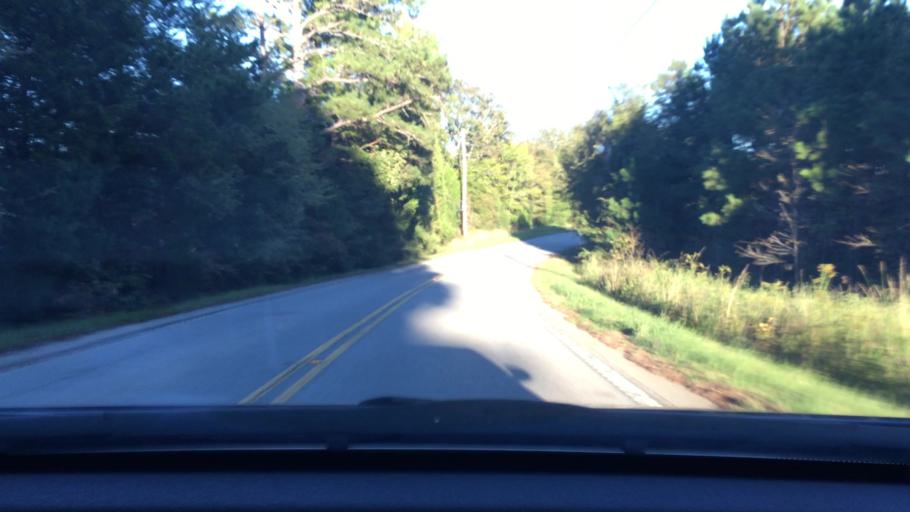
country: US
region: South Carolina
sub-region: Lexington County
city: Irmo
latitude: 34.1259
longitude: -81.1893
